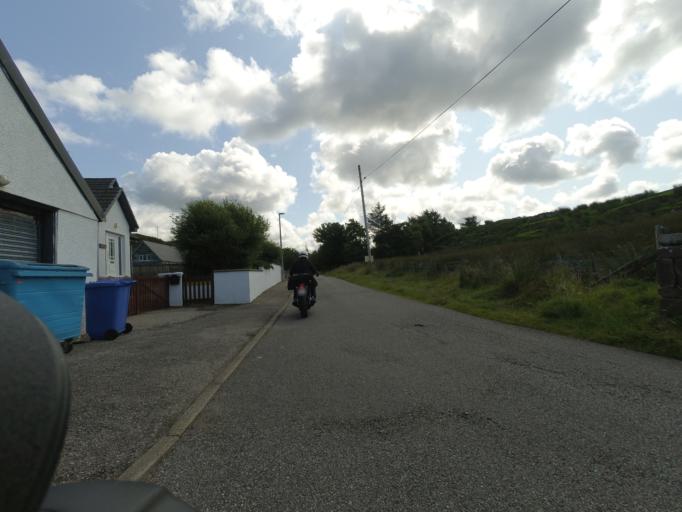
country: GB
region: Scotland
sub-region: Highland
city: Ullapool
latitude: 58.2432
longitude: -5.2018
